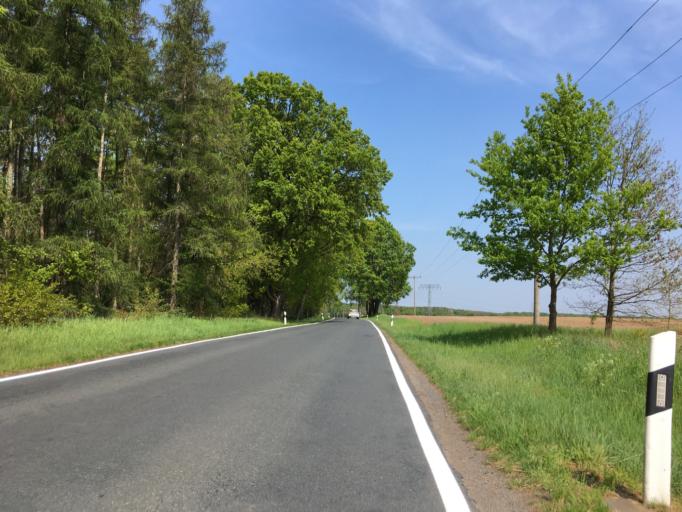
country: DE
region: Brandenburg
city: Melchow
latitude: 52.7158
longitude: 13.7137
